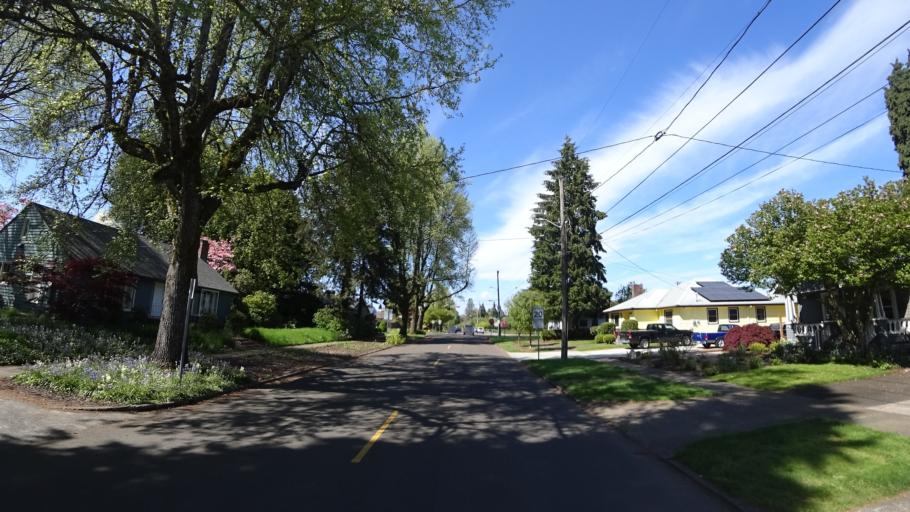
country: US
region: Oregon
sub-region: Washington County
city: Hillsboro
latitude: 45.5232
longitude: -122.9807
